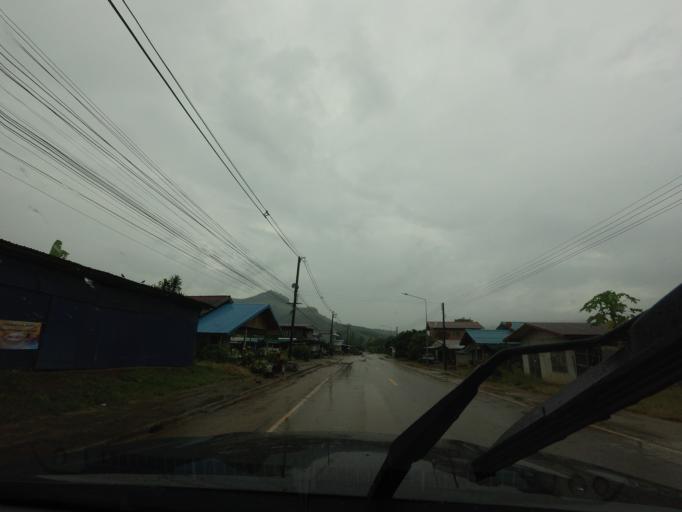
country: TH
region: Loei
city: Pak Chom
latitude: 18.1977
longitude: 102.0575
